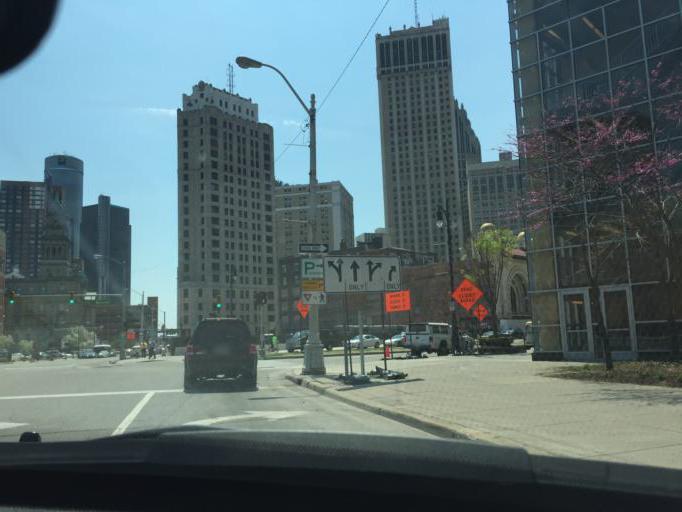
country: US
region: Michigan
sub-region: Wayne County
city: Detroit
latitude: 42.3342
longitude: -83.0451
